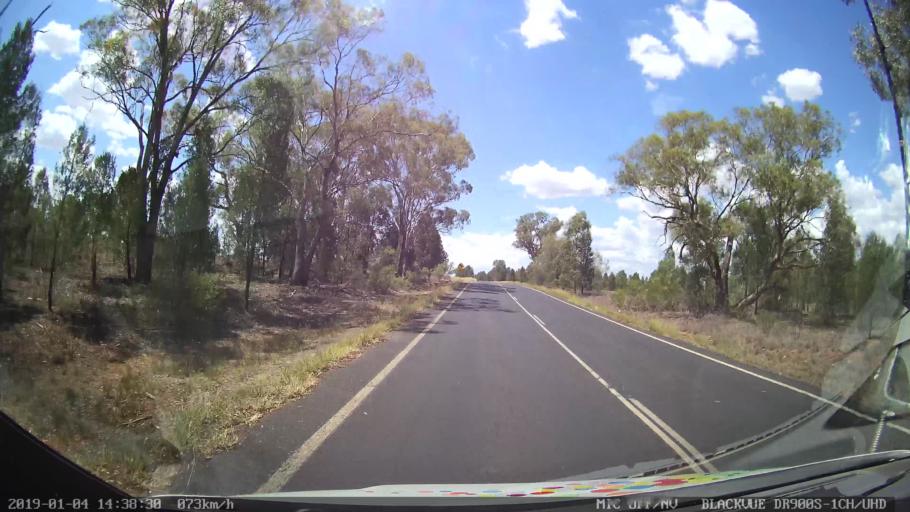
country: AU
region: New South Wales
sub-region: Dubbo Municipality
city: Dubbo
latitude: -32.1753
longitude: 148.6303
